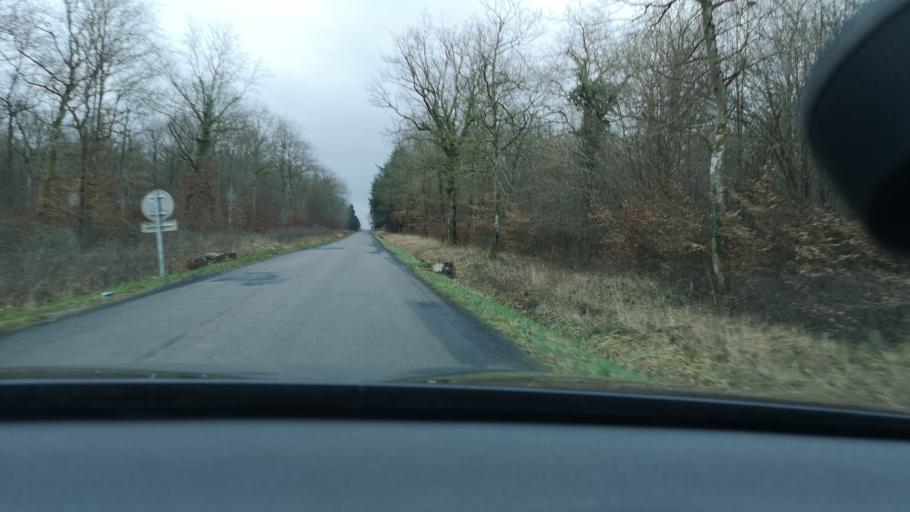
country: FR
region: Bourgogne
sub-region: Departement de Saone-et-Loire
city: Dracy-le-Fort
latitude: 46.7667
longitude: 4.7709
